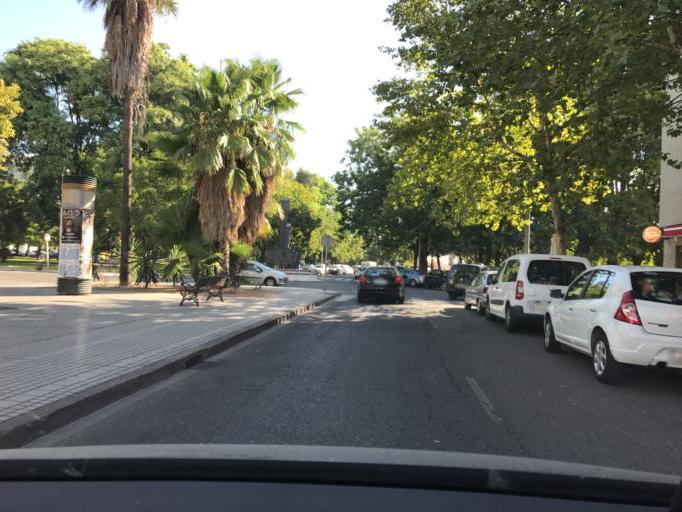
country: ES
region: Andalusia
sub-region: Province of Cordoba
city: Cordoba
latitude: 37.8885
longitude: -4.7967
